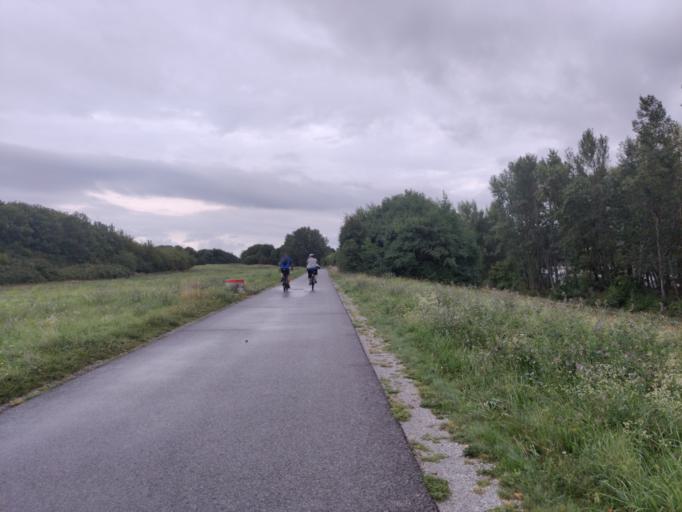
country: AT
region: Lower Austria
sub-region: Politischer Bezirk Korneuburg
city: Langenzersdorf
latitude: 48.2802
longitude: 16.3592
